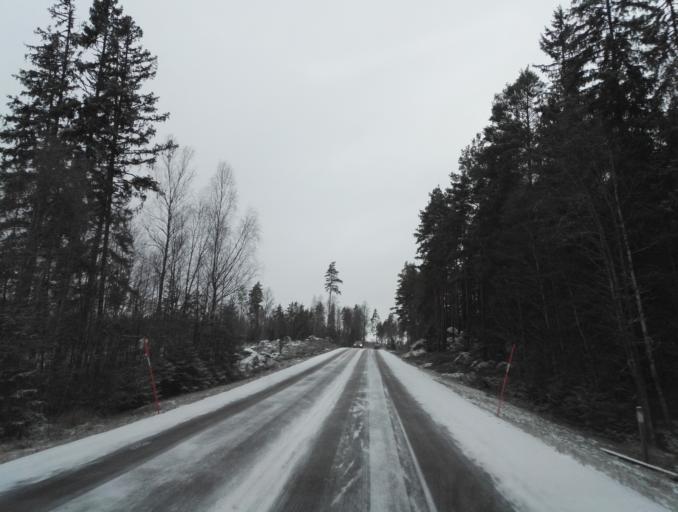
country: SE
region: Kronoberg
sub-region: Lessebo Kommun
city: Lessebo
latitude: 56.8037
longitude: 15.3506
